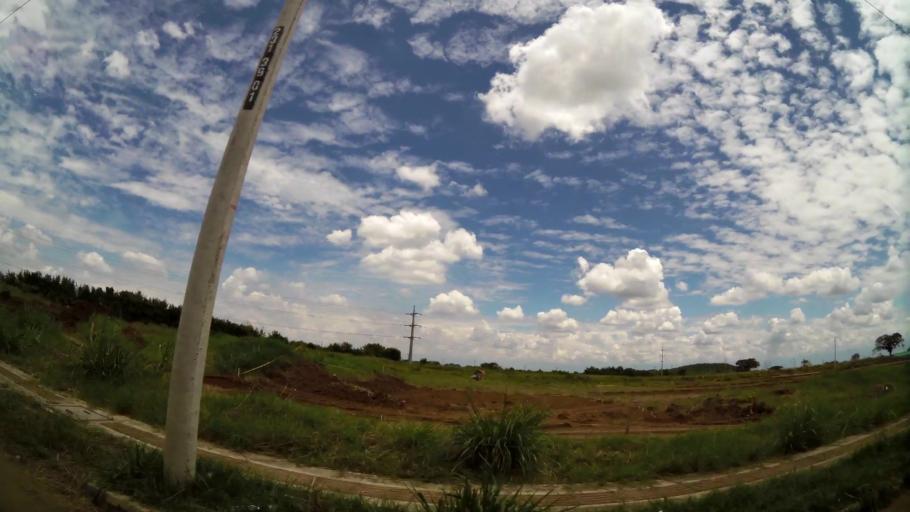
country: CO
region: Valle del Cauca
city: Cali
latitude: 3.3839
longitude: -76.5098
